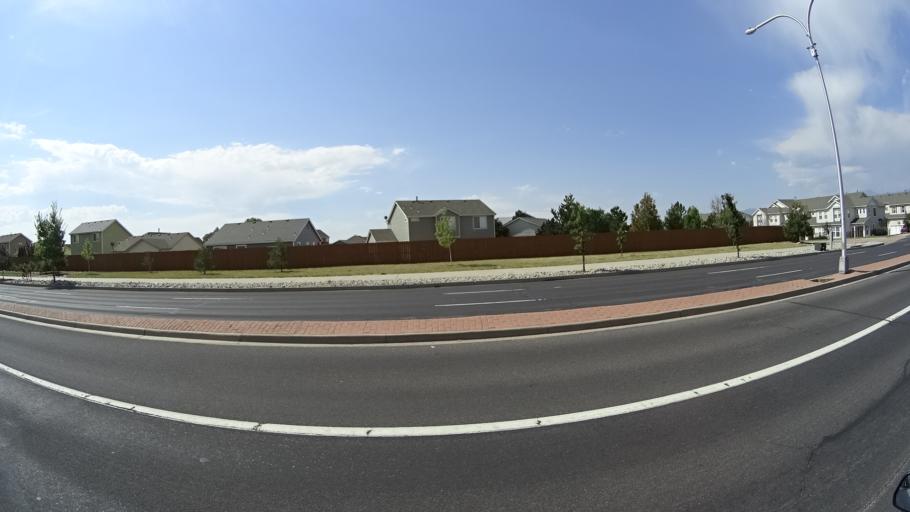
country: US
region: Colorado
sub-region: El Paso County
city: Cimarron Hills
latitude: 38.9260
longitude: -104.7101
